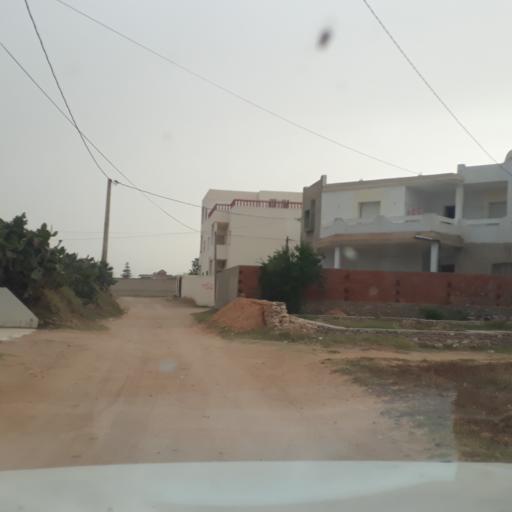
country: TN
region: Safaqis
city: Al Qarmadah
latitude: 34.8206
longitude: 10.7720
